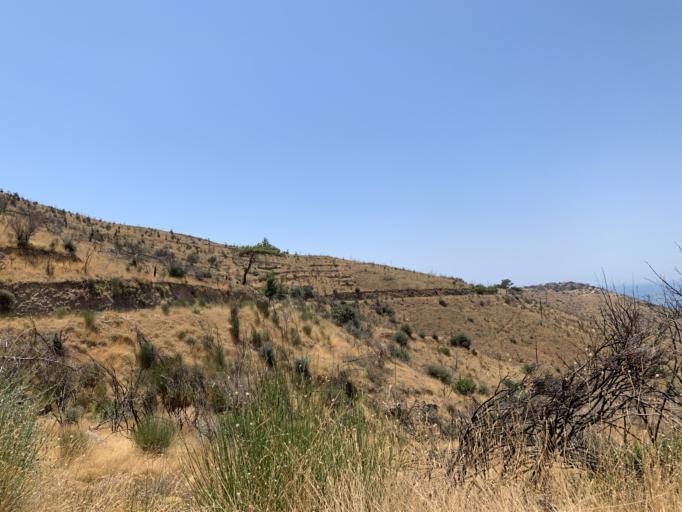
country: GR
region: North Aegean
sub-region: Chios
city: Vrontados
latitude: 38.4430
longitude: 25.9775
